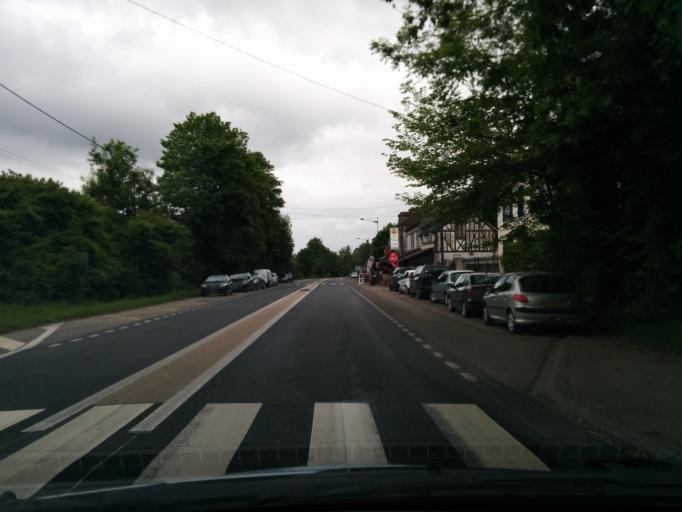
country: FR
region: Ile-de-France
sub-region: Departement des Yvelines
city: Limetz-Villez
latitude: 49.0771
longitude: 1.5092
